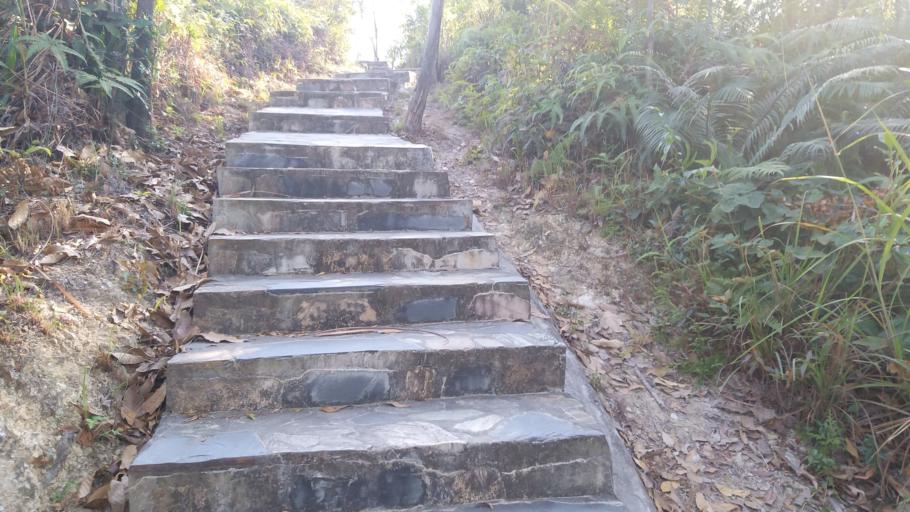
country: HK
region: Tuen Mun
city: Tuen Mun
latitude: 22.4019
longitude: 113.9882
